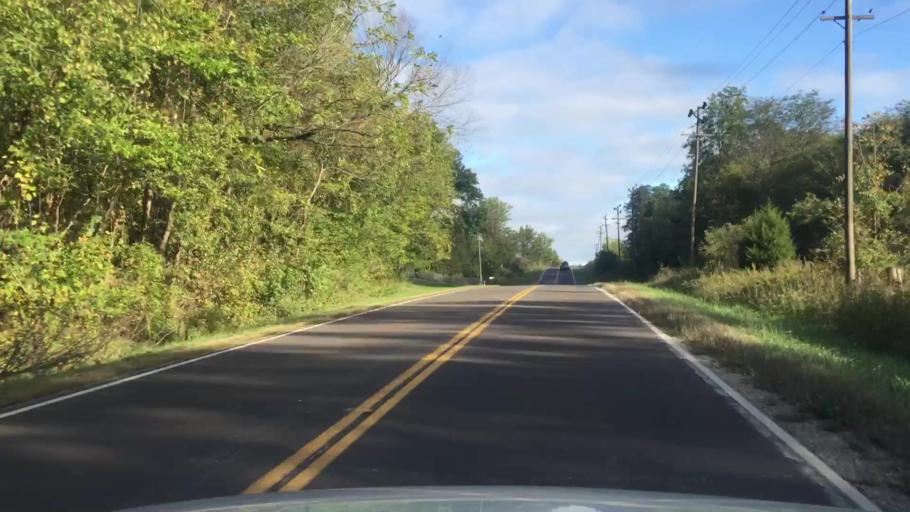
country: US
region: Missouri
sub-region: Howard County
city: New Franklin
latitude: 39.0498
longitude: -92.7444
